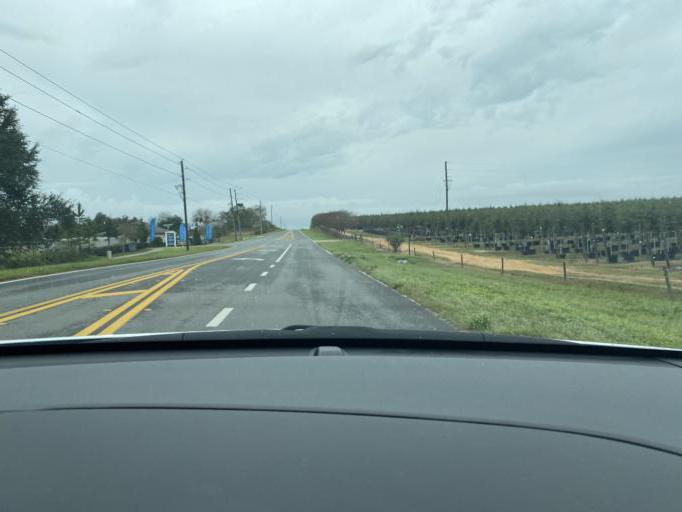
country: US
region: Florida
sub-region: Lake County
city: Groveland
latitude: 28.5874
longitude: -81.8425
